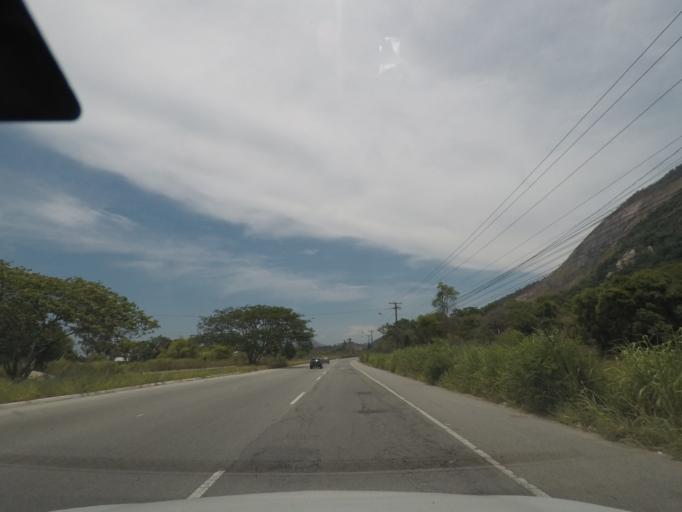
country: BR
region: Rio de Janeiro
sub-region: Marica
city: Marica
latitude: -22.9356
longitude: -42.9067
